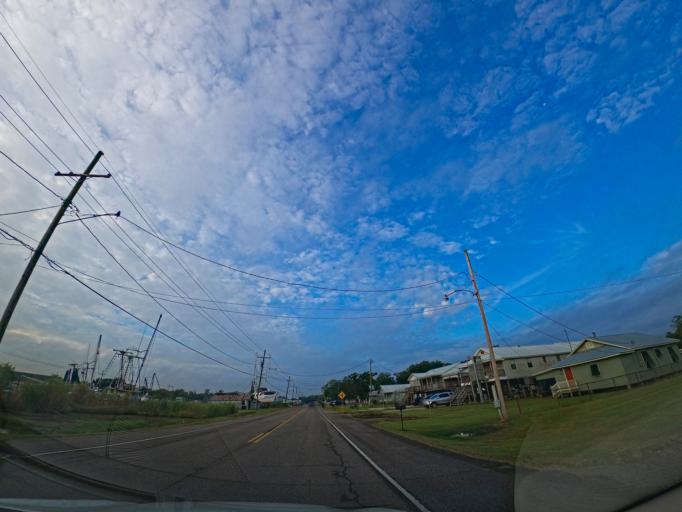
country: US
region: Louisiana
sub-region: Terrebonne Parish
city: Chauvin
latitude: 29.4284
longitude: -90.5994
